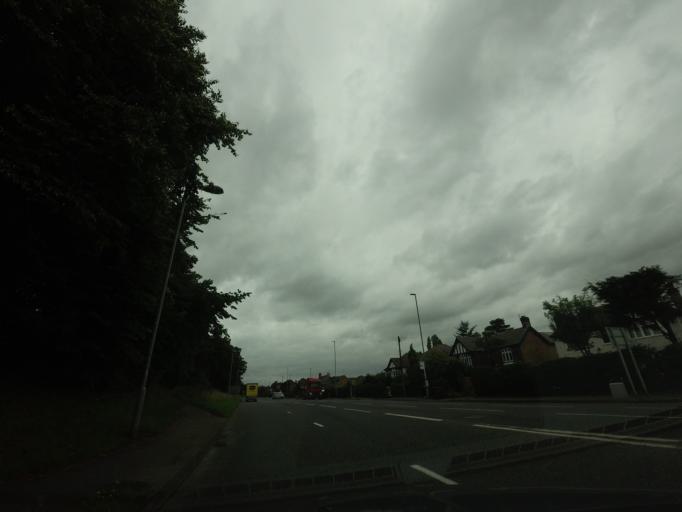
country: GB
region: England
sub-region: Nottinghamshire
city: Kimberley
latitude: 52.9913
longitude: -1.2244
